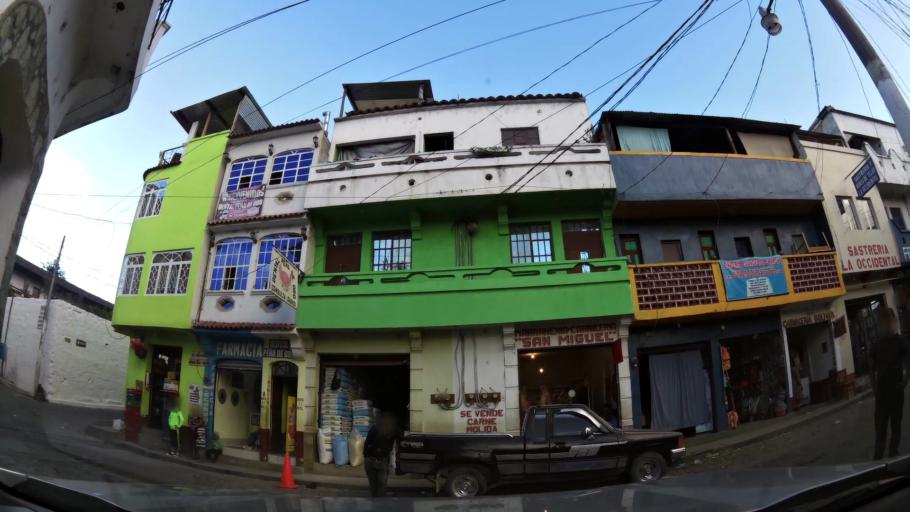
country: GT
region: Quiche
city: Chichicastenango
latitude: 14.9415
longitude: -91.1120
